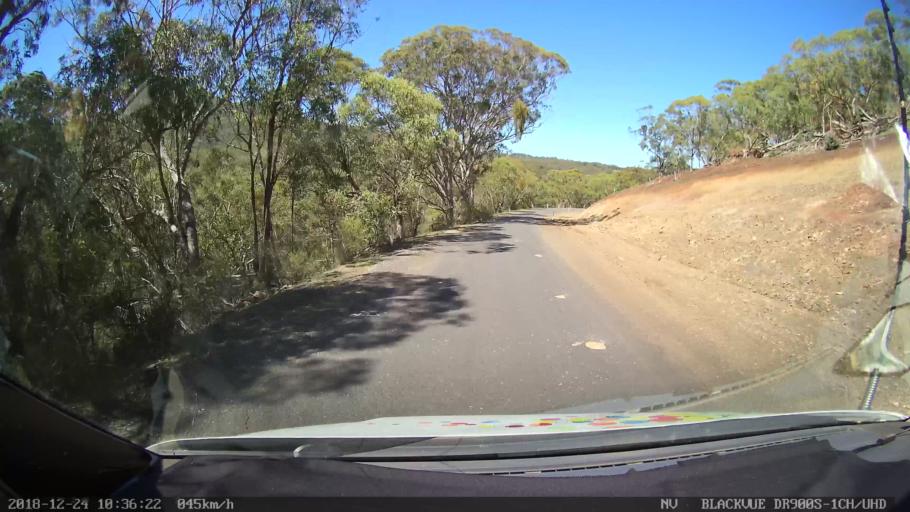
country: AU
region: New South Wales
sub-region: Upper Hunter Shire
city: Merriwa
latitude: -31.8441
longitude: 150.5002
